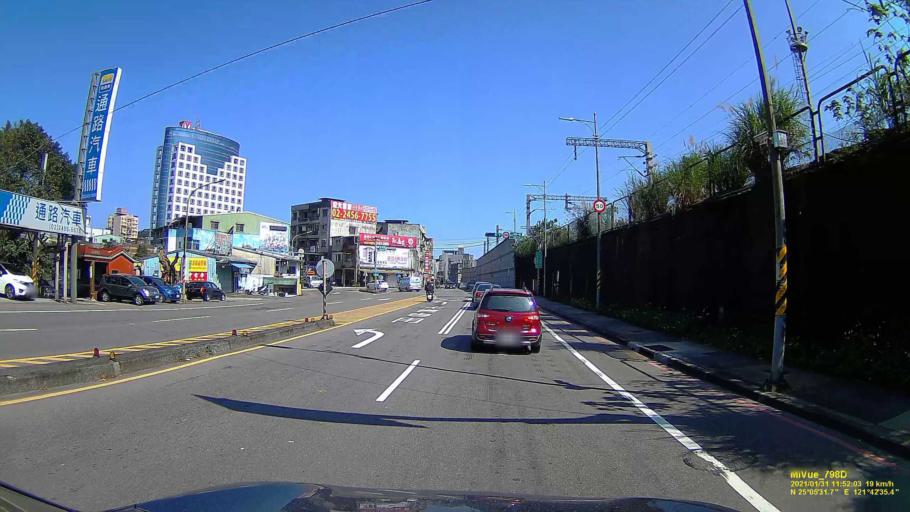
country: TW
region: Taiwan
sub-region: Keelung
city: Keelung
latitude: 25.0922
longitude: 121.7099
